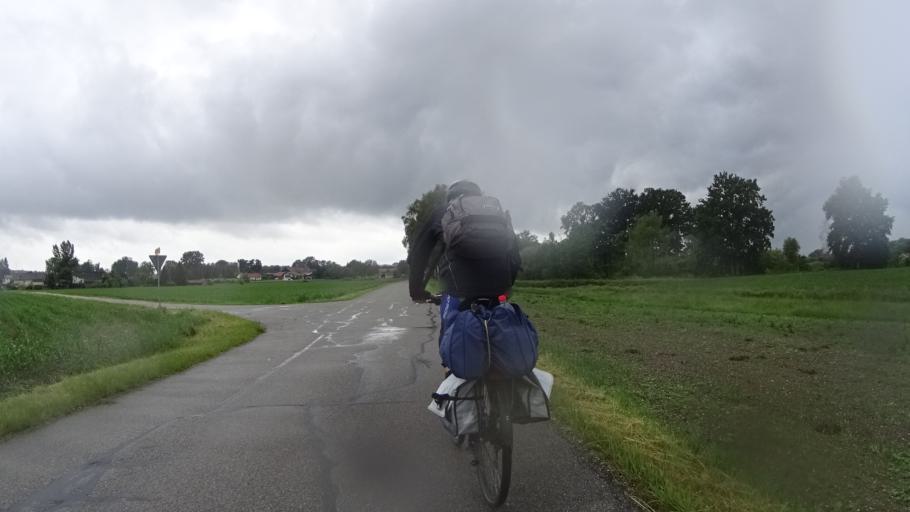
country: DE
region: Bavaria
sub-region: Lower Bavaria
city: Tettenweis
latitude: 48.4101
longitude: 13.2729
